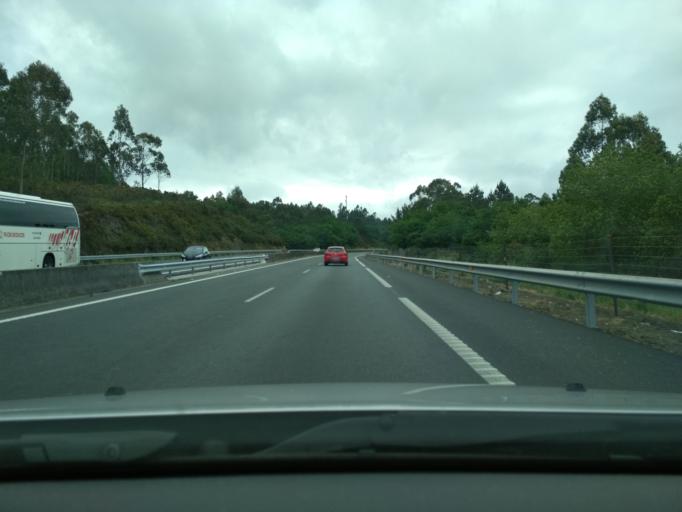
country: ES
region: Galicia
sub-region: Provincia da Coruna
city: Santiago de Compostela
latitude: 42.8433
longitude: -8.5718
